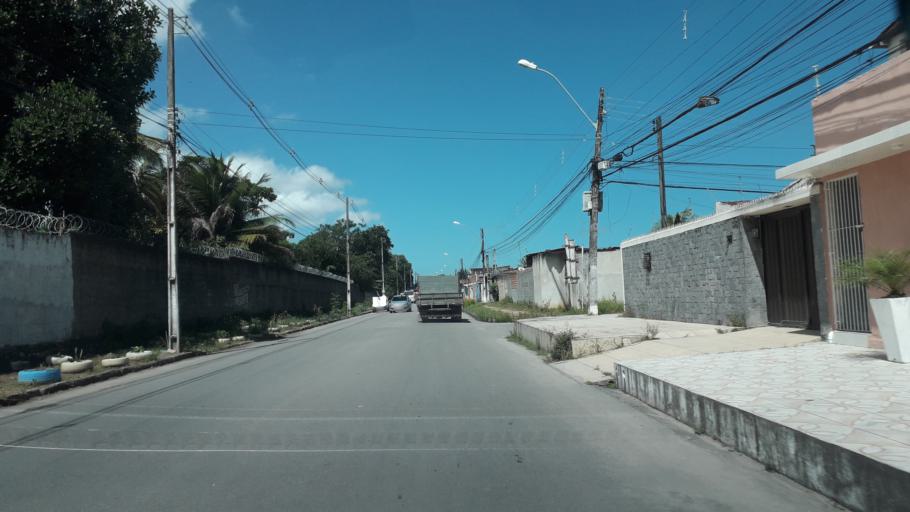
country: BR
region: Alagoas
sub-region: Satuba
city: Satuba
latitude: -9.5581
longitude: -35.7835
